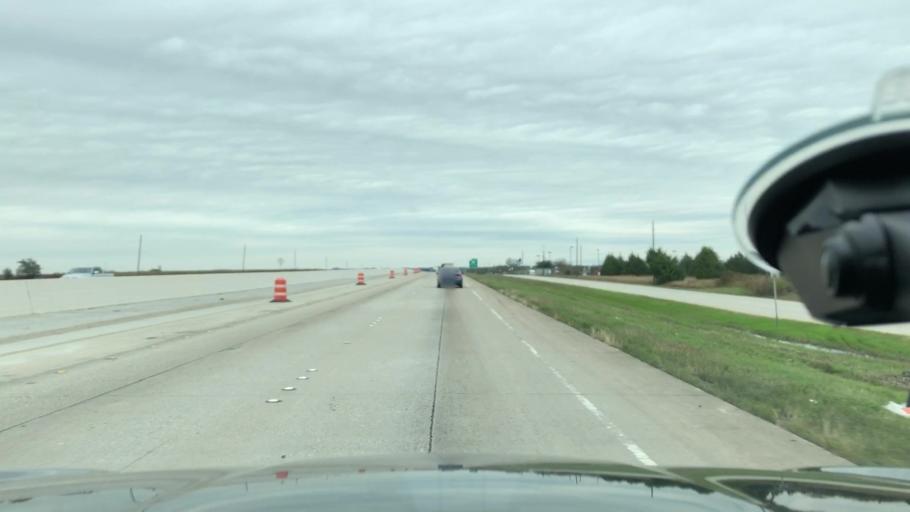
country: US
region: Texas
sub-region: Ellis County
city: Oak Leaf
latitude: 32.4808
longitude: -96.8324
